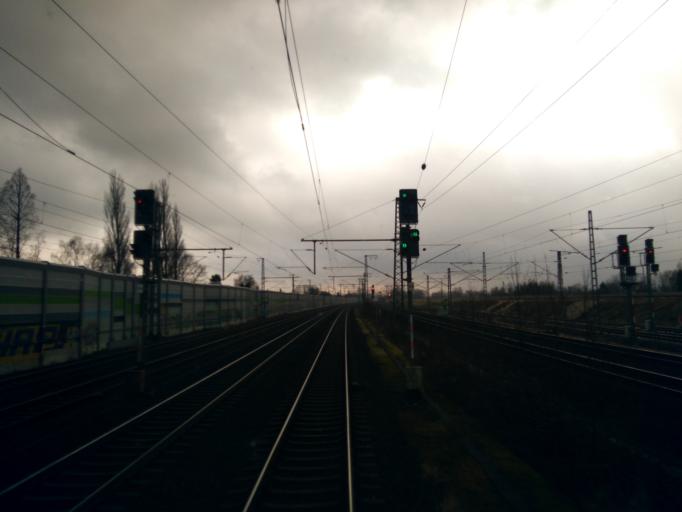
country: DE
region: Hamburg
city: Harburg
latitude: 53.4885
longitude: 10.0044
